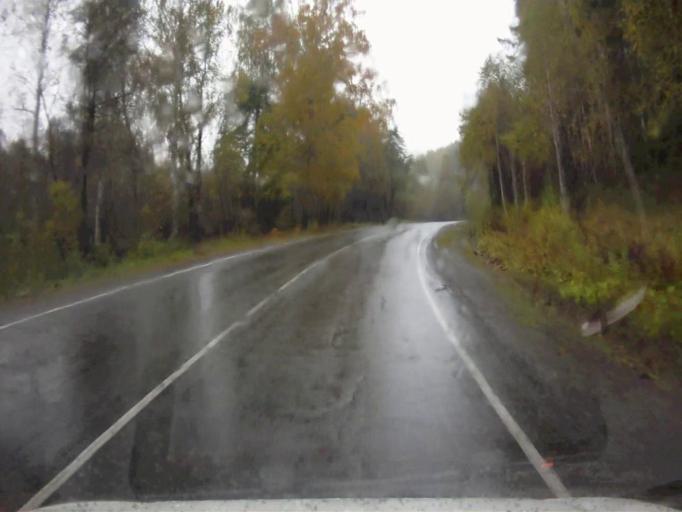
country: RU
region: Chelyabinsk
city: Kyshtym
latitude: 55.9069
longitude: 60.4396
